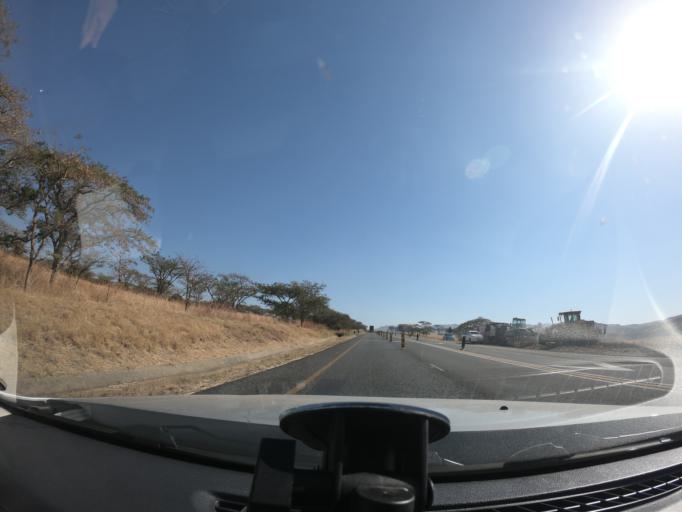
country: ZA
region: KwaZulu-Natal
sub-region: uThukela District Municipality
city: Ladysmith
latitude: -28.4379
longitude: 29.4872
